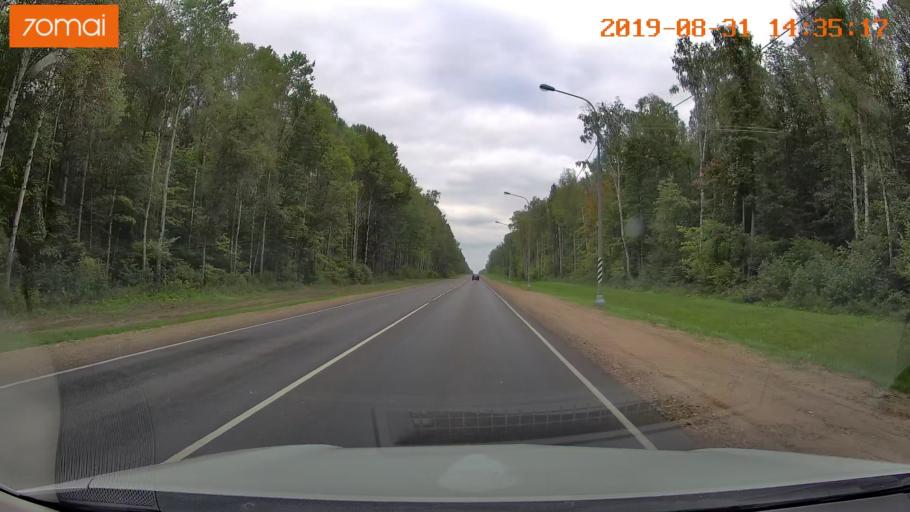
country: RU
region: Smolensk
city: Yekimovichi
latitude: 54.1618
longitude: 33.4523
